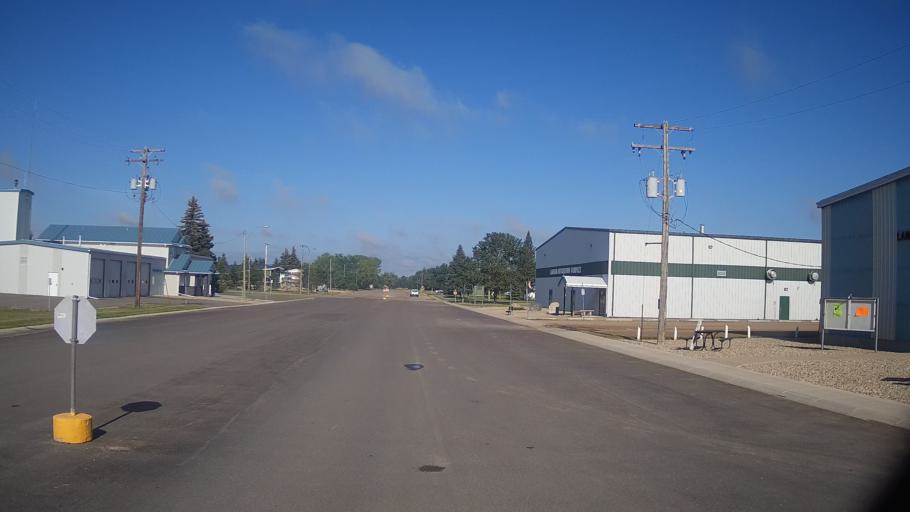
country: CA
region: Saskatchewan
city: Lanigan
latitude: 51.8509
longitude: -105.0289
